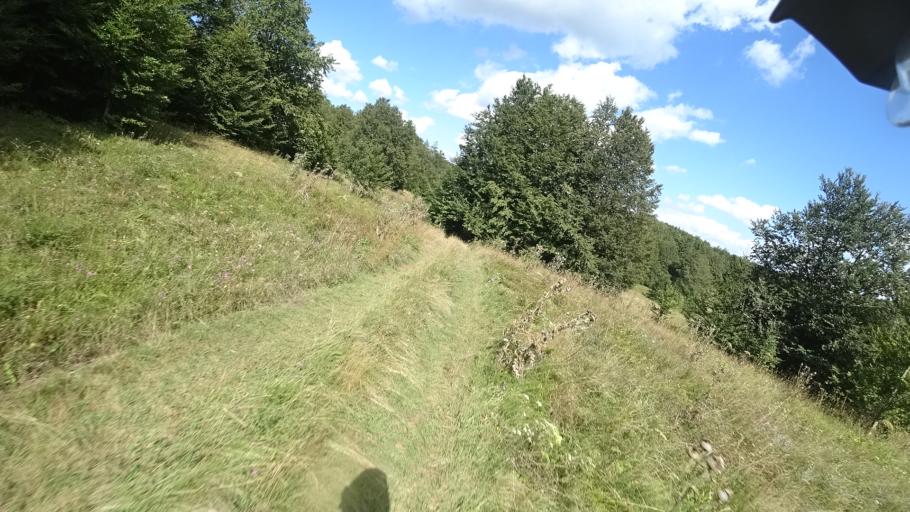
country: HR
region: Zadarska
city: Gracac
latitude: 44.4297
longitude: 15.9949
